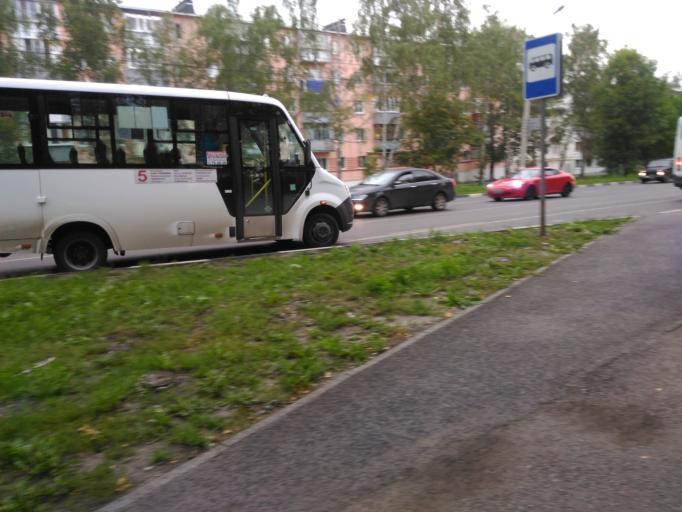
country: RU
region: Ulyanovsk
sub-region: Ulyanovskiy Rayon
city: Ulyanovsk
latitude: 54.2637
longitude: 48.3348
